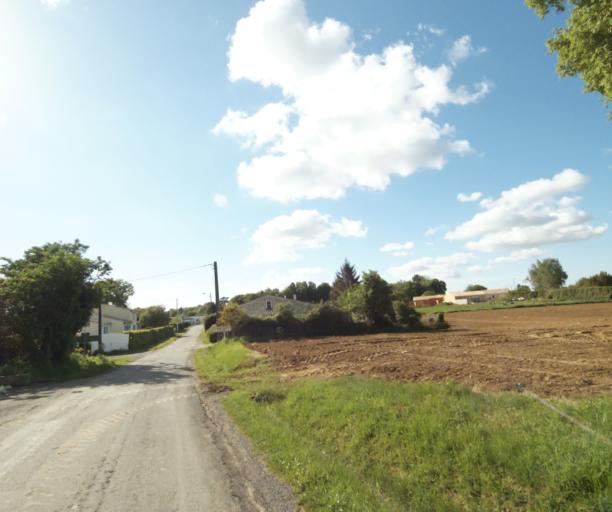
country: FR
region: Poitou-Charentes
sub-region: Departement de la Charente-Maritime
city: Nieul-les-Saintes
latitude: 45.7067
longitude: -0.7453
